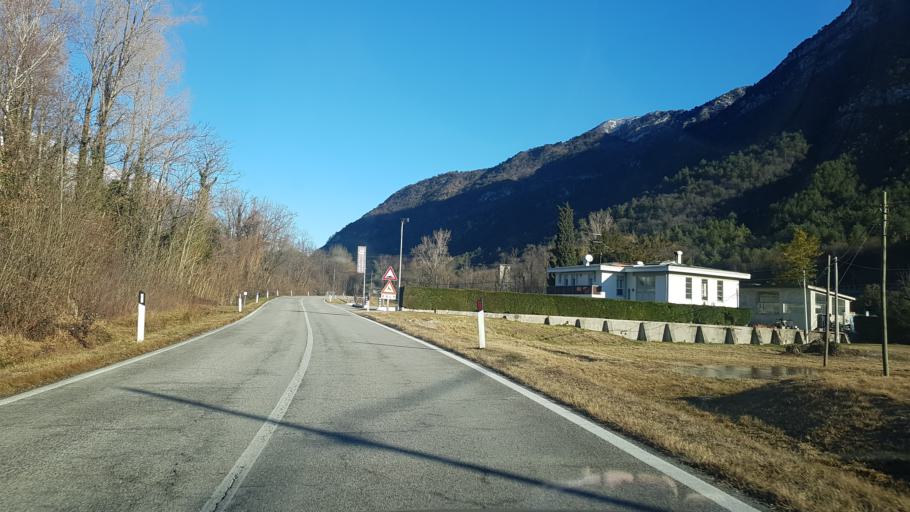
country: IT
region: Friuli Venezia Giulia
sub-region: Provincia di Udine
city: Trasaghis
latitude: 46.2876
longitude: 13.0644
